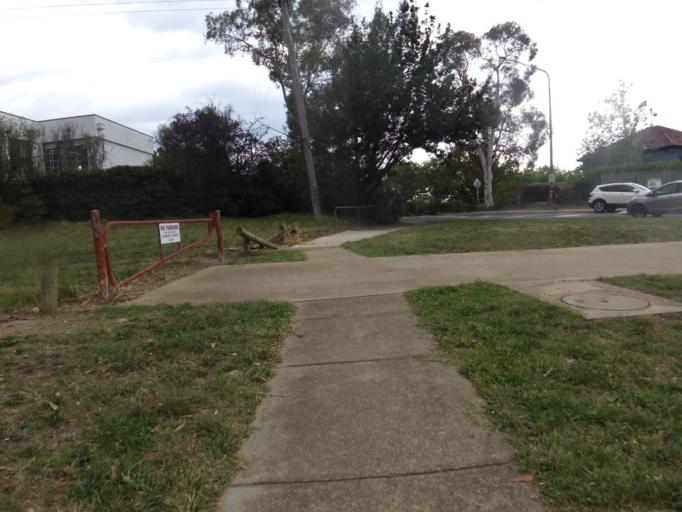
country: AU
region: Australian Capital Territory
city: Forrest
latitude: -35.3428
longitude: 149.1383
